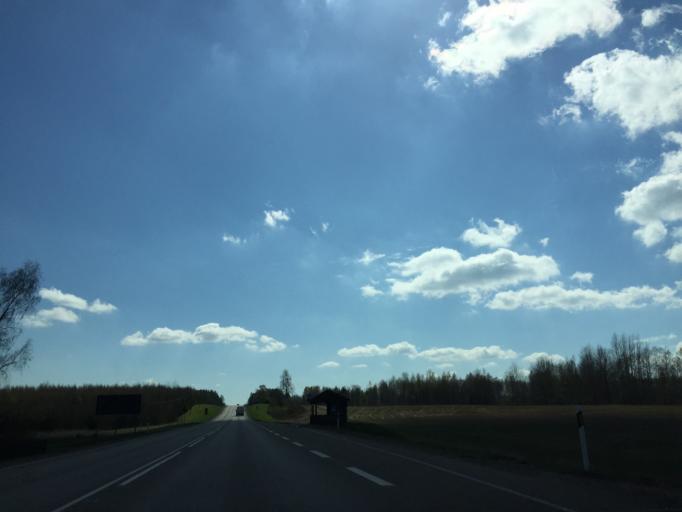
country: EE
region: Tartu
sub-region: Elva linn
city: Elva
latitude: 58.0816
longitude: 26.2086
